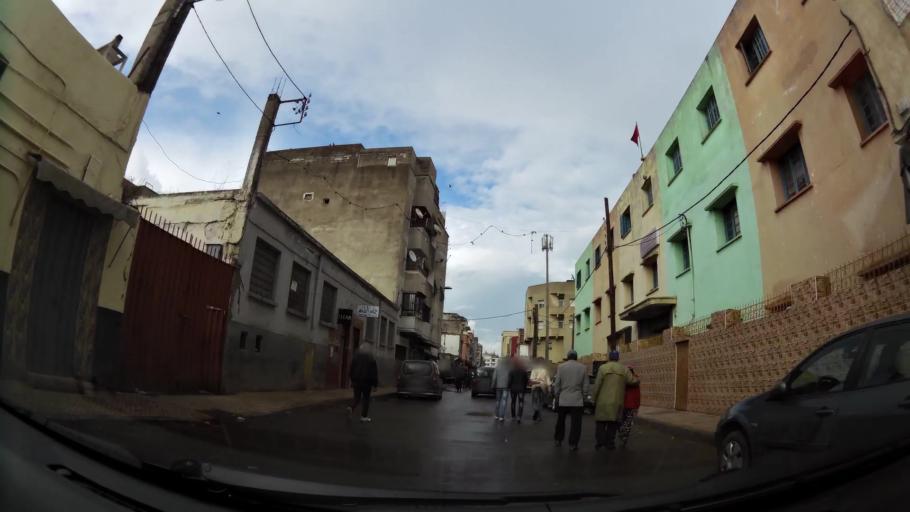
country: MA
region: Grand Casablanca
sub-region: Casablanca
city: Casablanca
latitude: 33.5722
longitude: -7.6009
